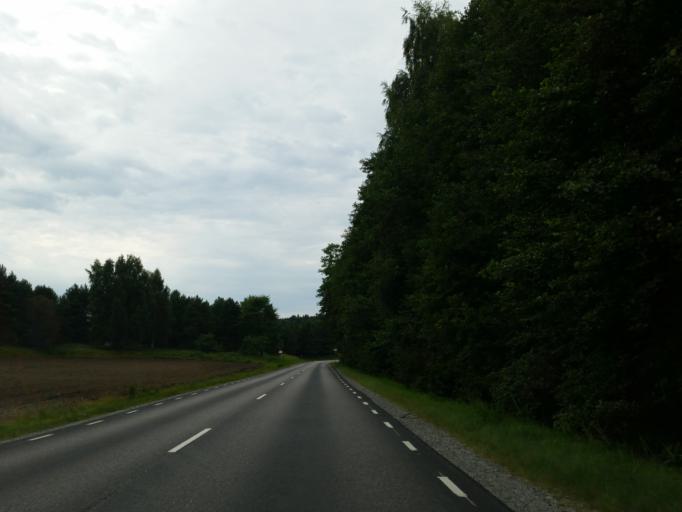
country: SE
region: Stockholm
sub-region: Botkyrka Kommun
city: Eriksberg
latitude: 59.2190
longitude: 17.7798
